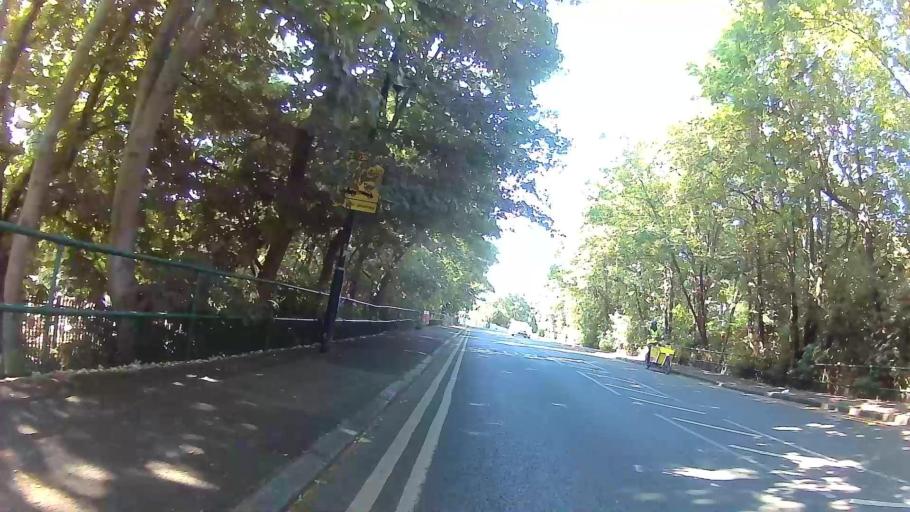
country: GB
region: England
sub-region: Greater London
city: East Ham
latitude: 51.5267
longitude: 0.0178
